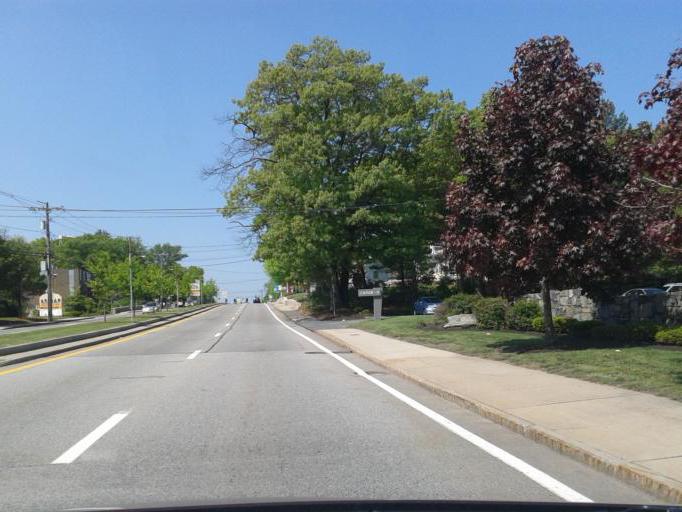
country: US
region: Massachusetts
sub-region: Middlesex County
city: Framingham
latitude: 42.3028
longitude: -71.4027
